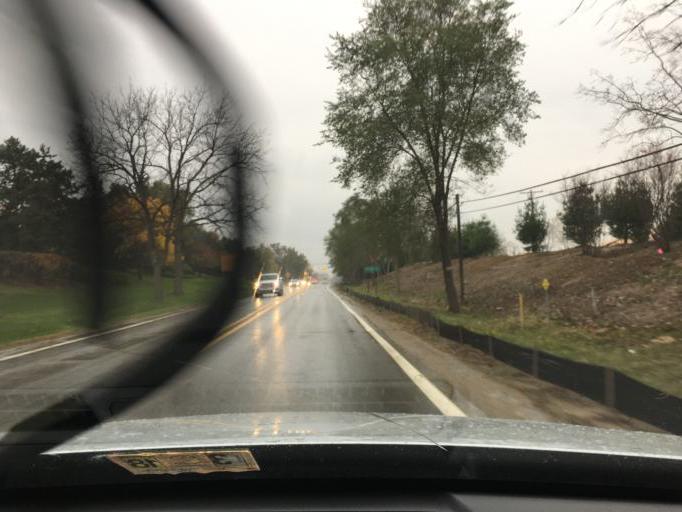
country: US
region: Michigan
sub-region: Oakland County
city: Auburn Hills
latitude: 42.7123
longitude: -83.1956
